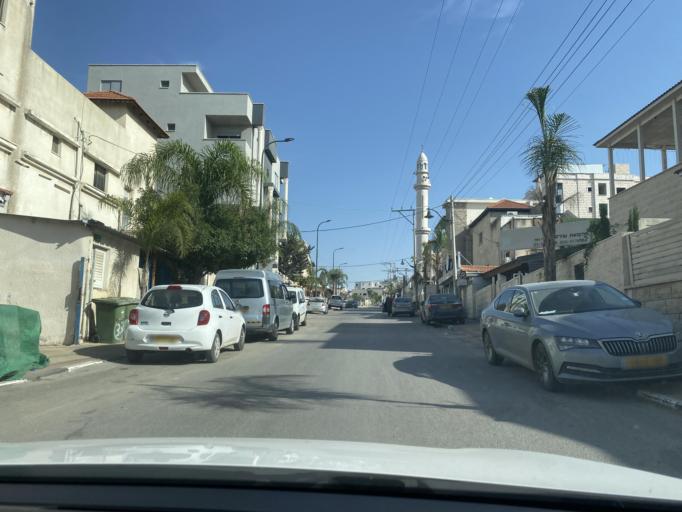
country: IL
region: Central District
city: Kafr Qasim
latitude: 32.1314
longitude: 34.9678
